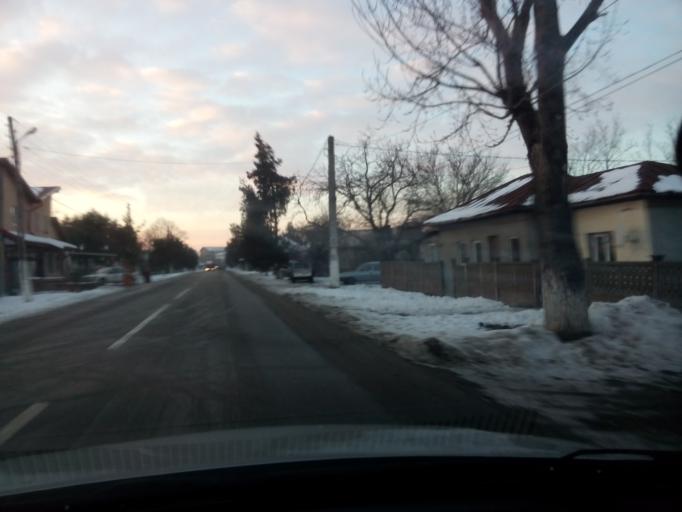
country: RO
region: Calarasi
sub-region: Comuna Budesti
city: Budesti
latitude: 44.2337
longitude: 26.4684
